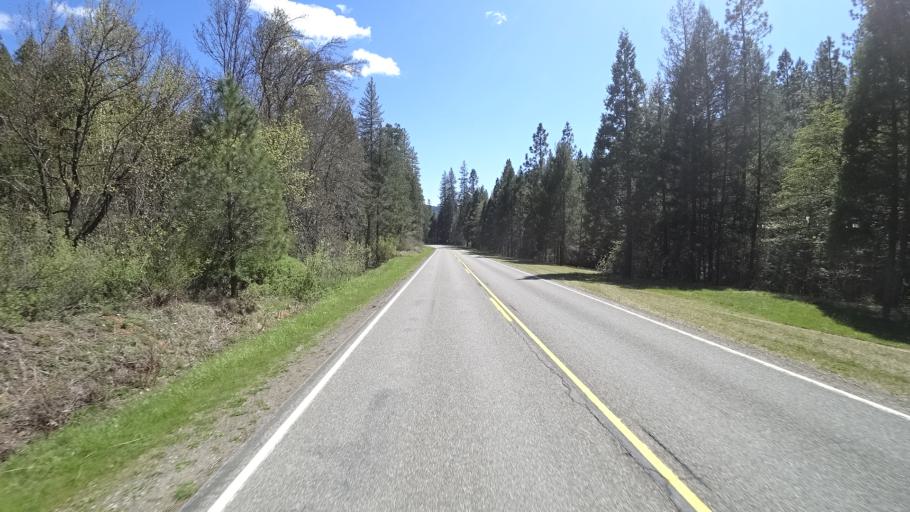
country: US
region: California
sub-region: Trinity County
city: Weaverville
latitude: 40.7719
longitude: -122.8915
